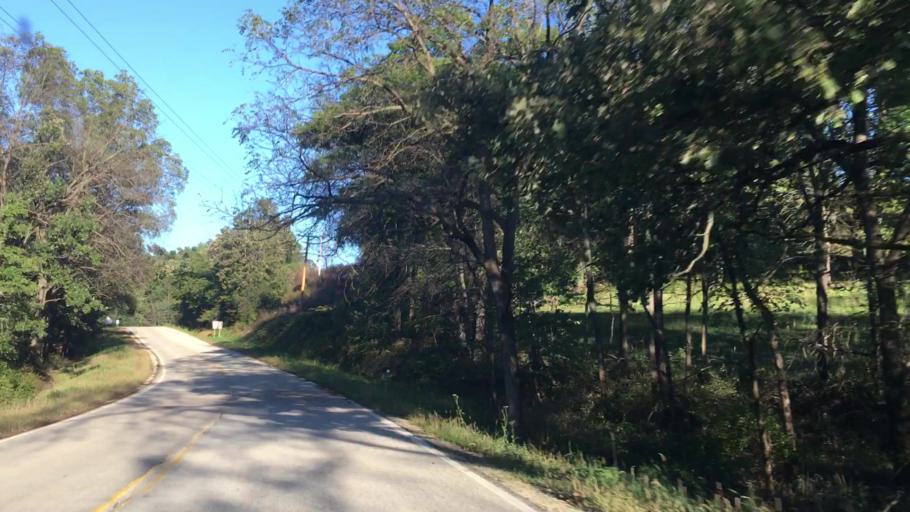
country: US
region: Minnesota
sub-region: Fillmore County
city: Chatfield
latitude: 43.8180
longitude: -92.0421
